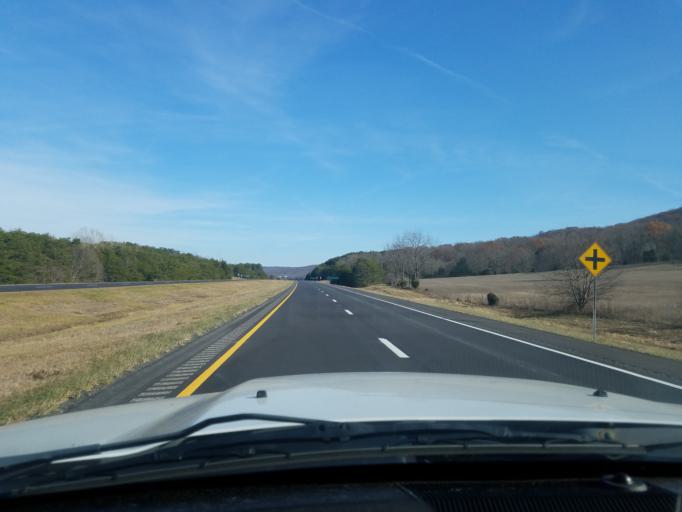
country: US
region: Ohio
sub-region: Adams County
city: Peebles
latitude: 38.9807
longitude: -83.3280
